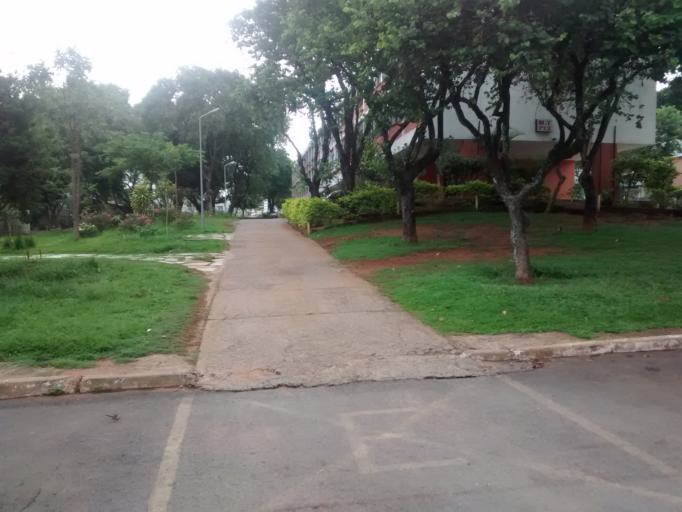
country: BR
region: Federal District
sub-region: Brasilia
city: Brasilia
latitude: -15.7531
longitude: -47.8962
